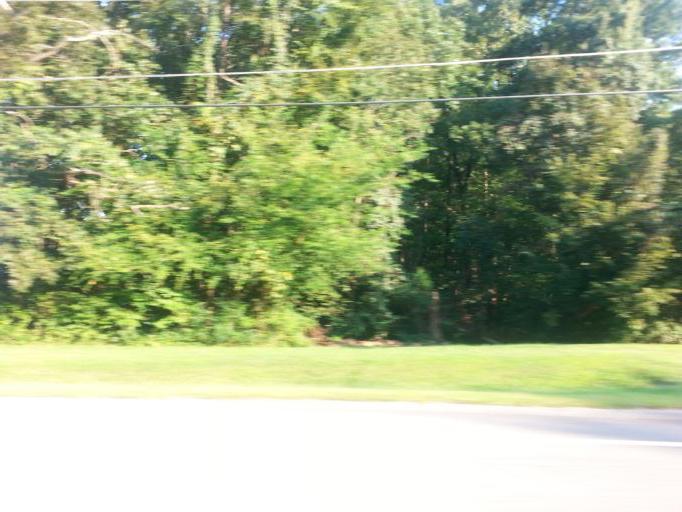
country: US
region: Tennessee
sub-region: Knox County
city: Knoxville
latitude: 35.9102
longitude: -83.8360
